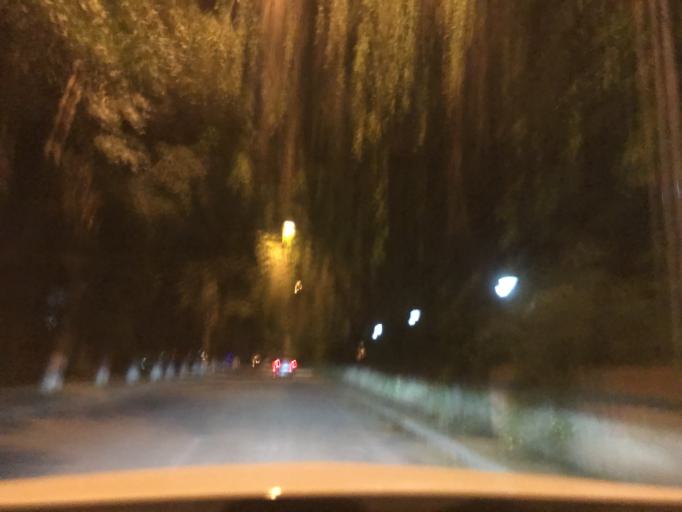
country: CN
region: Sichuan
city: Mianyang
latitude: 31.4493
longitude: 104.7553
